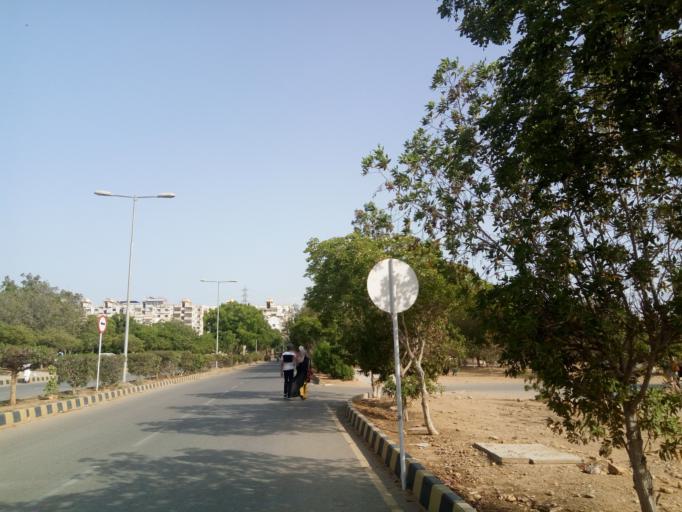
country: PK
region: Sindh
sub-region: Karachi District
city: Karachi
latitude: 24.9315
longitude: 67.1146
